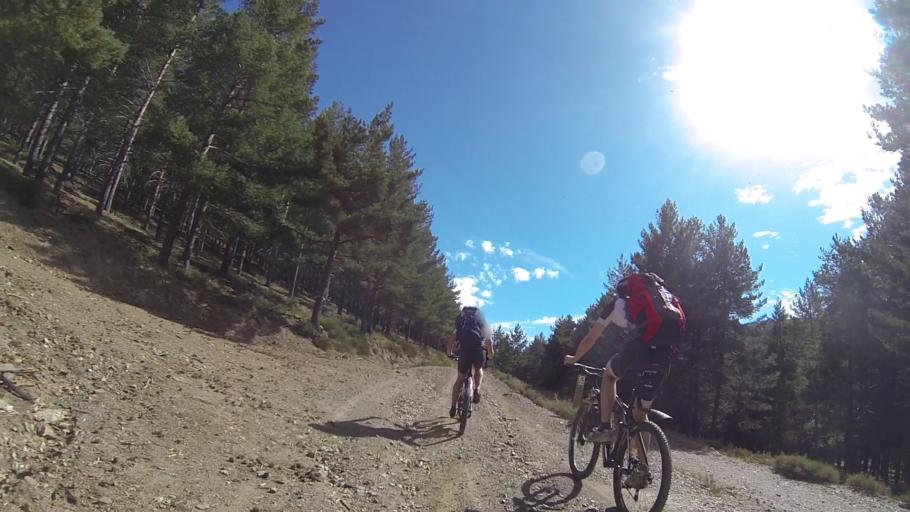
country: ES
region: Andalusia
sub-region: Provincia de Granada
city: Ferreira
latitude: 37.1126
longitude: -3.0271
